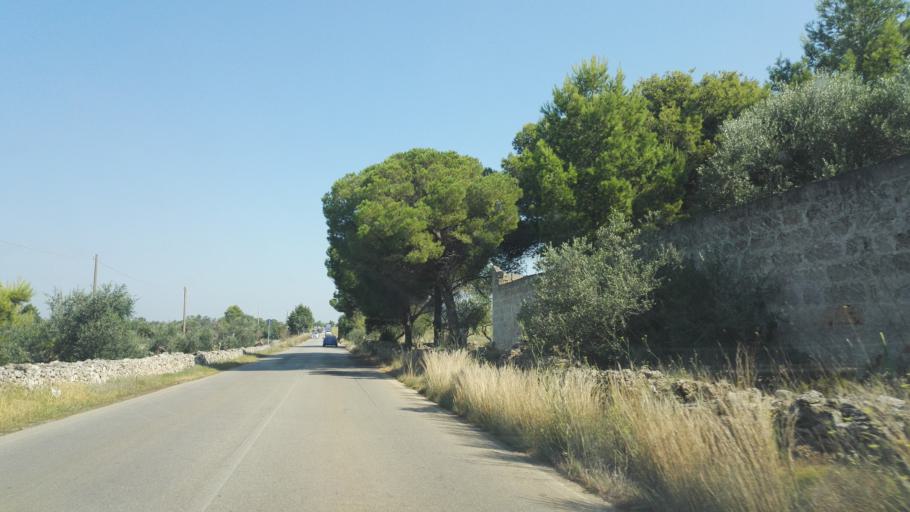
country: IT
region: Apulia
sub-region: Provincia di Lecce
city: Nardo
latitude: 40.1124
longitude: 18.0218
